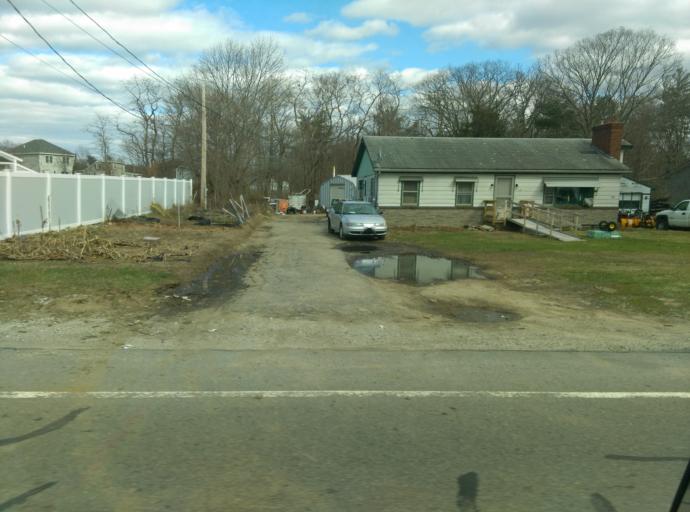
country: US
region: New Hampshire
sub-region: Rockingham County
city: Seabrook
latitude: 42.8675
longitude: -70.8866
